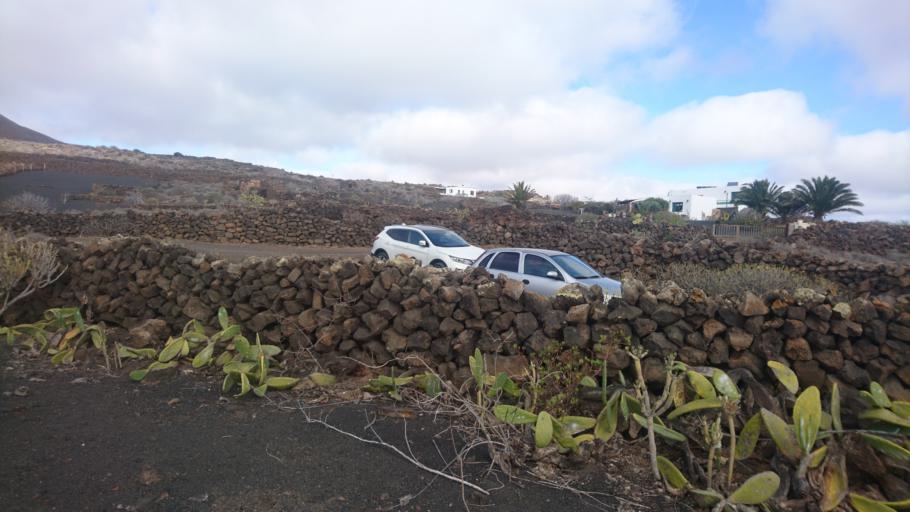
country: ES
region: Canary Islands
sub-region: Provincia de Las Palmas
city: Haria
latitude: 29.1760
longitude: -13.4653
